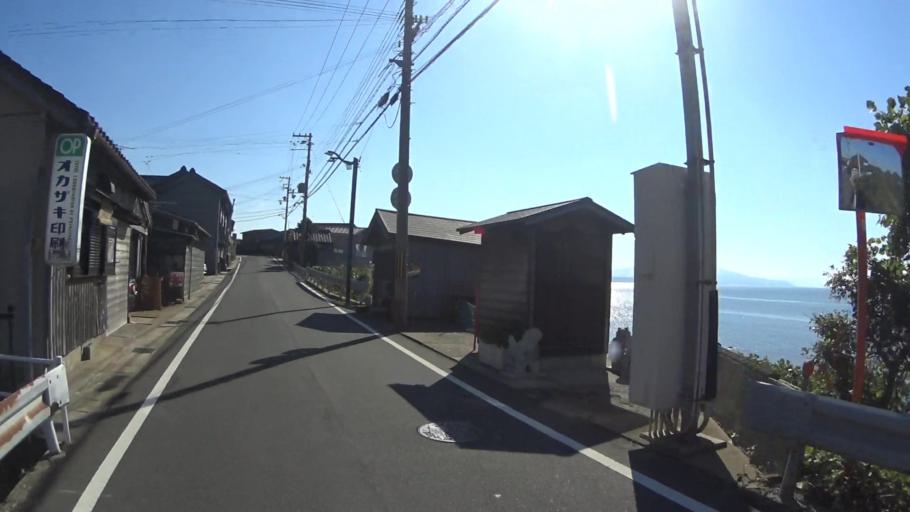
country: JP
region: Kyoto
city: Miyazu
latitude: 35.7356
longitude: 135.0856
